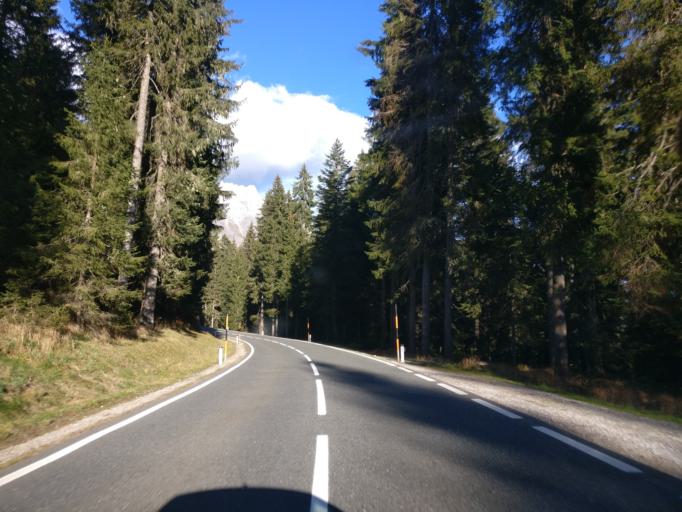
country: AT
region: Salzburg
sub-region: Politischer Bezirk Zell am See
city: Dienten am Hochkonig
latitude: 47.3921
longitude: 13.0674
